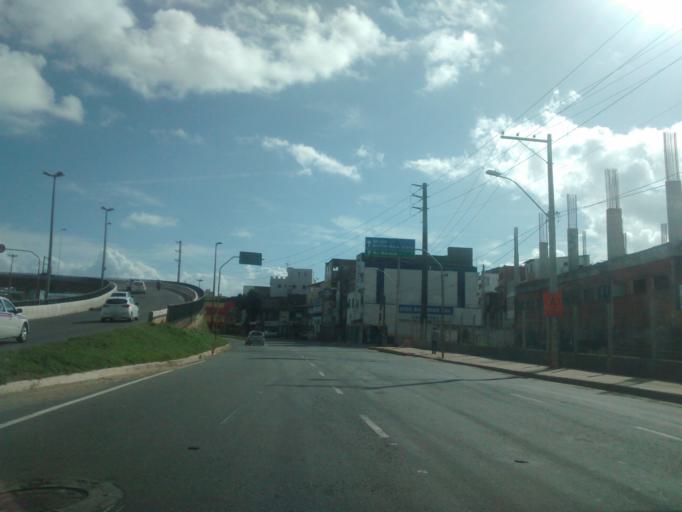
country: BR
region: Bahia
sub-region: Salvador
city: Salvador
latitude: -12.9752
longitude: -38.4587
